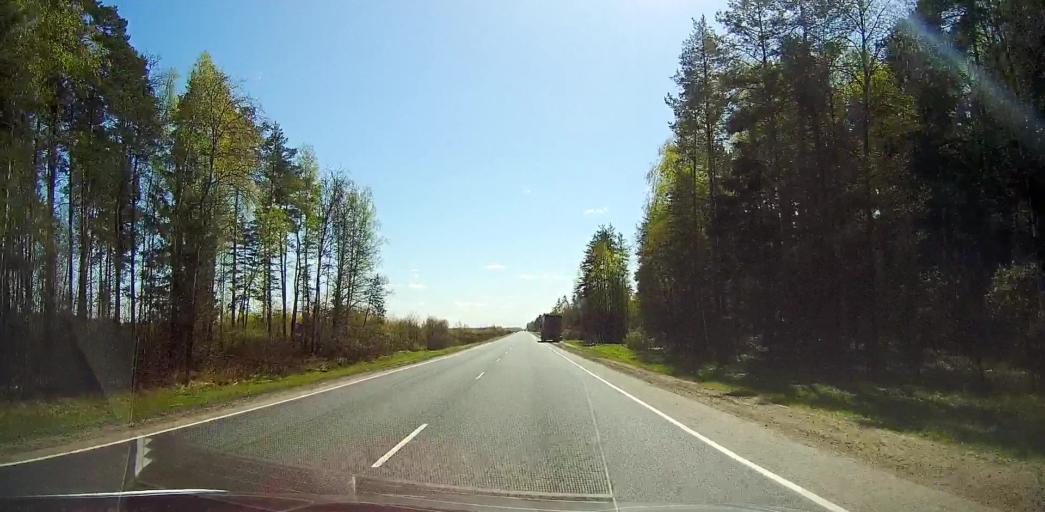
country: RU
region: Moskovskaya
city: Gzhel'
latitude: 55.6000
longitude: 38.3788
